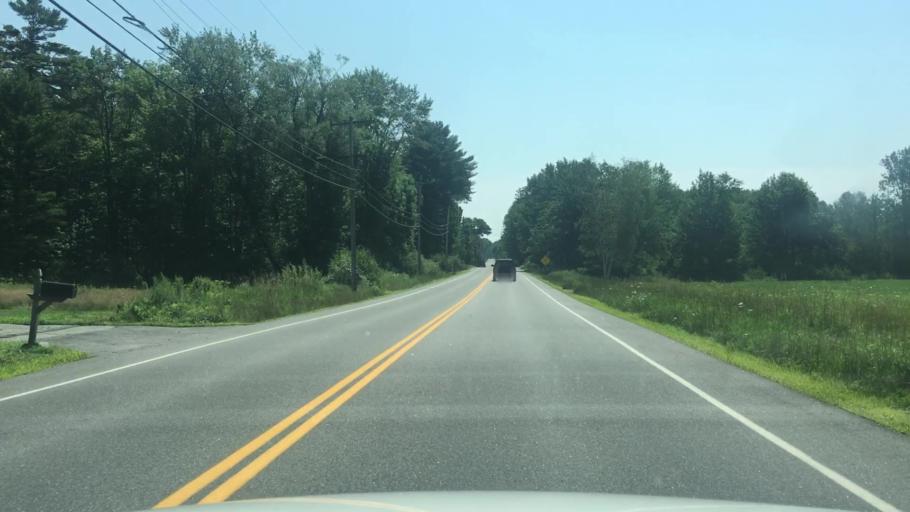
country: US
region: Maine
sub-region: Cumberland County
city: Cumberland Center
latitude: 43.8079
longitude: -70.2814
